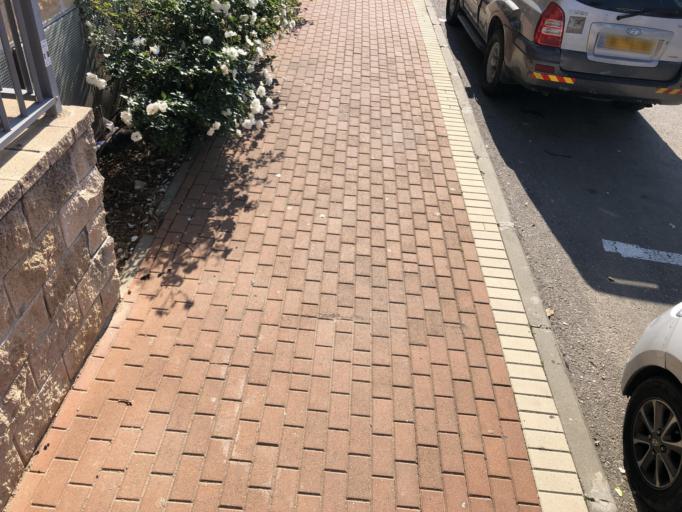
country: IL
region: Northern District
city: `Akko
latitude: 32.9290
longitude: 35.0959
